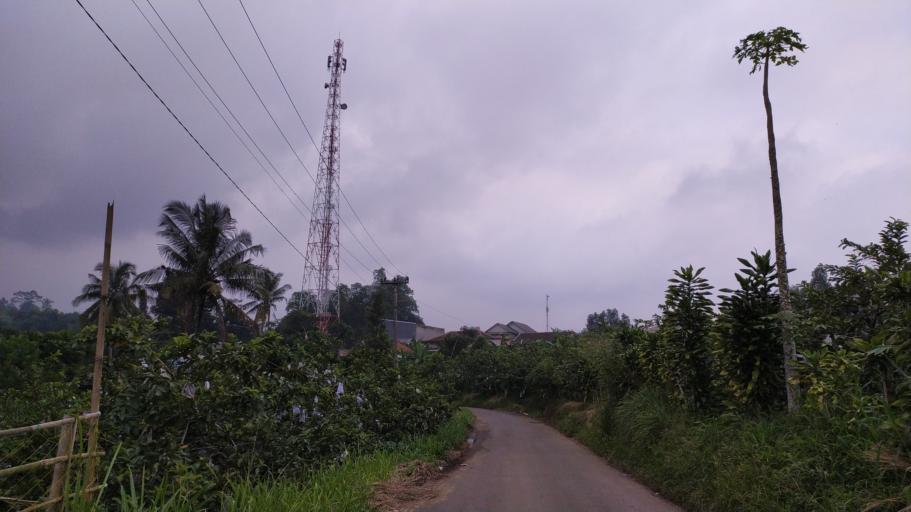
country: ID
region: West Java
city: Ciampea
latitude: -6.6411
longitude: 106.7066
